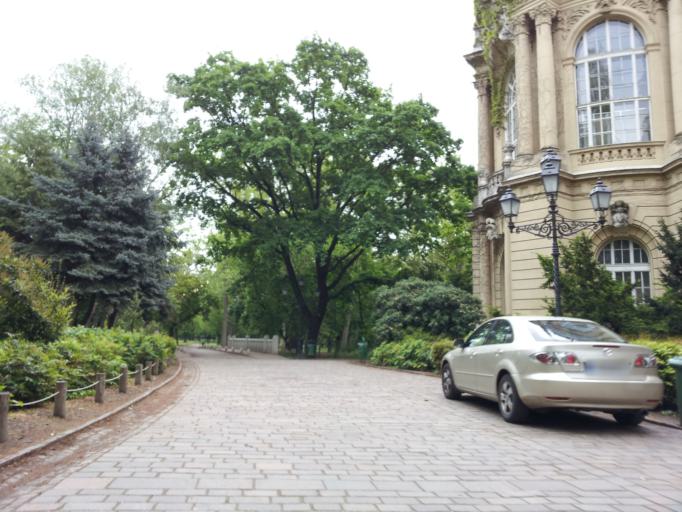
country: HU
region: Budapest
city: Budapest XIII. keruelet
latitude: 47.5155
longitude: 19.0830
